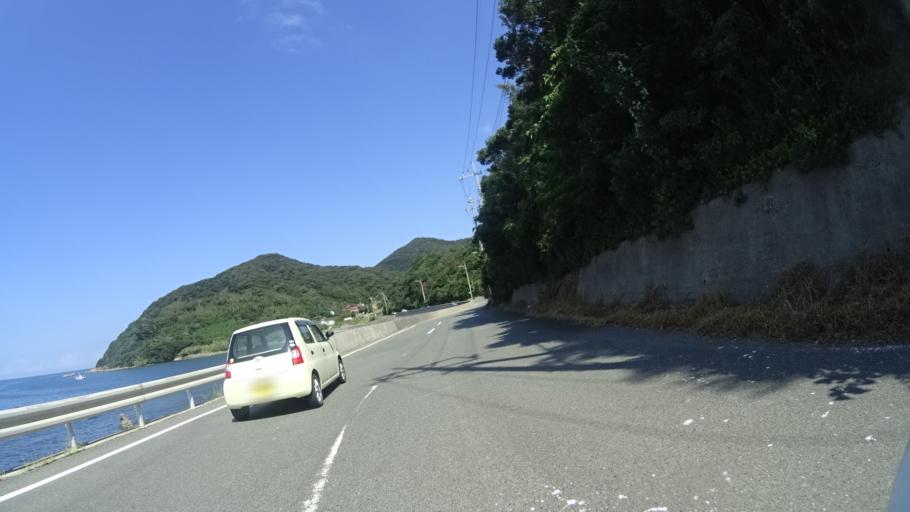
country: JP
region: Yamaguchi
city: Shimonoseki
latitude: 34.1000
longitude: 130.8705
